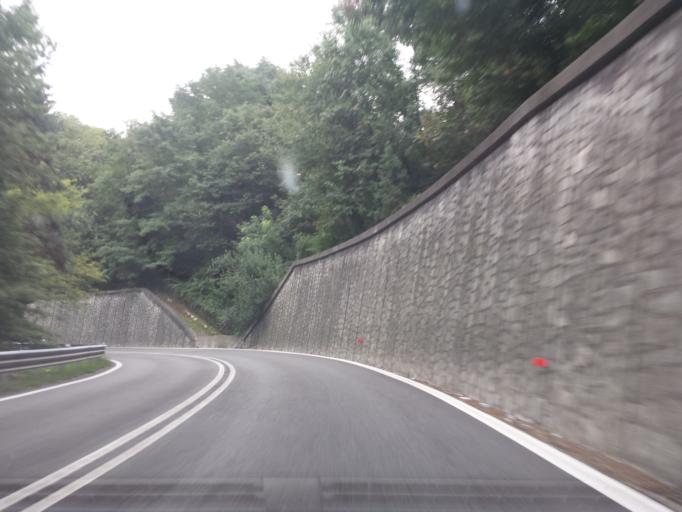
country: IT
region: Lombardy
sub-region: Provincia di Varese
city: Golasecca
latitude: 45.7180
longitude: 8.6689
